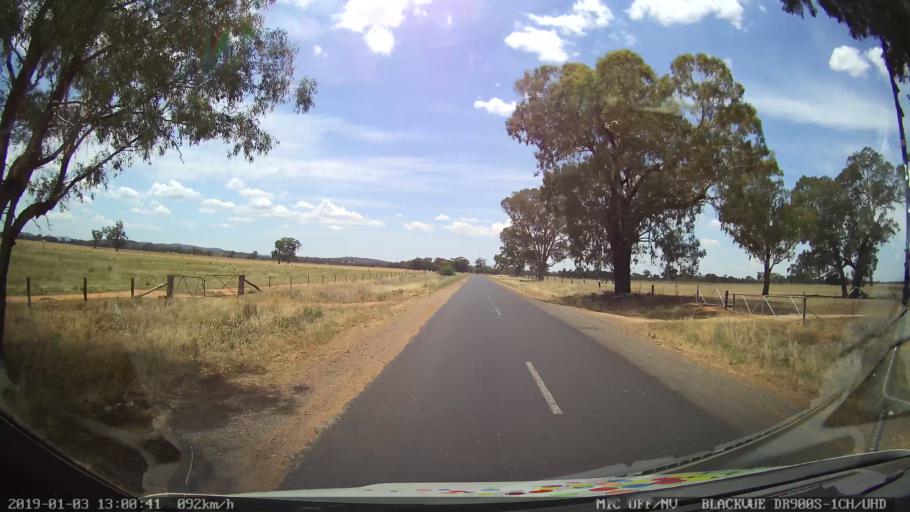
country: AU
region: New South Wales
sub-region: Cabonne
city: Canowindra
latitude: -33.6295
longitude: 148.4075
